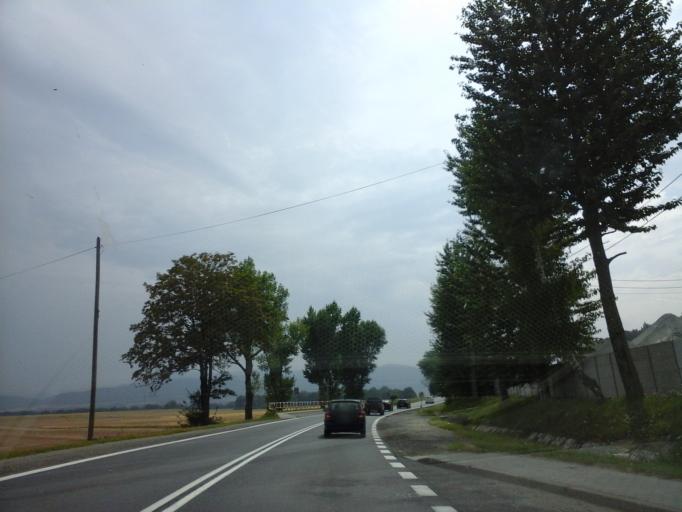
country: PL
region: Lower Silesian Voivodeship
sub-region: Powiat zabkowicki
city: Zabkowice Slaskie
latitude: 50.5437
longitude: 16.7988
